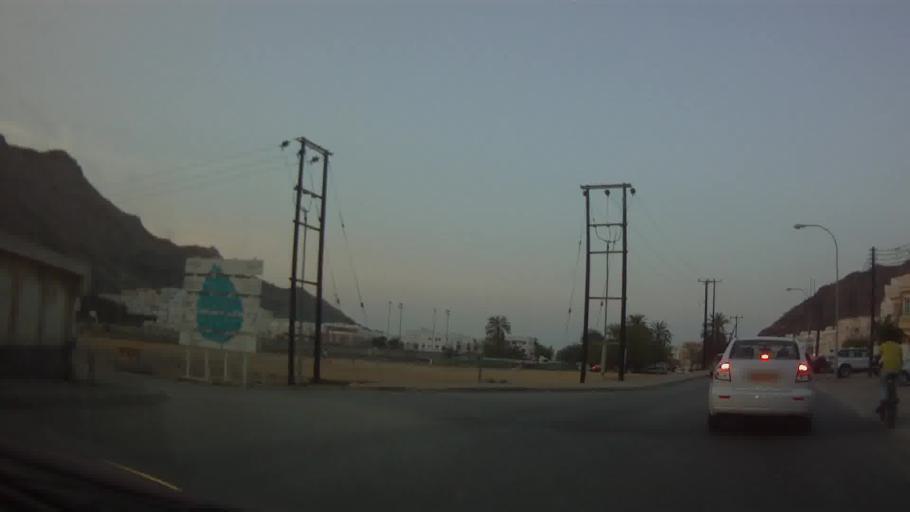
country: OM
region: Muhafazat Masqat
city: Muscat
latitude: 23.6221
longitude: 58.5404
